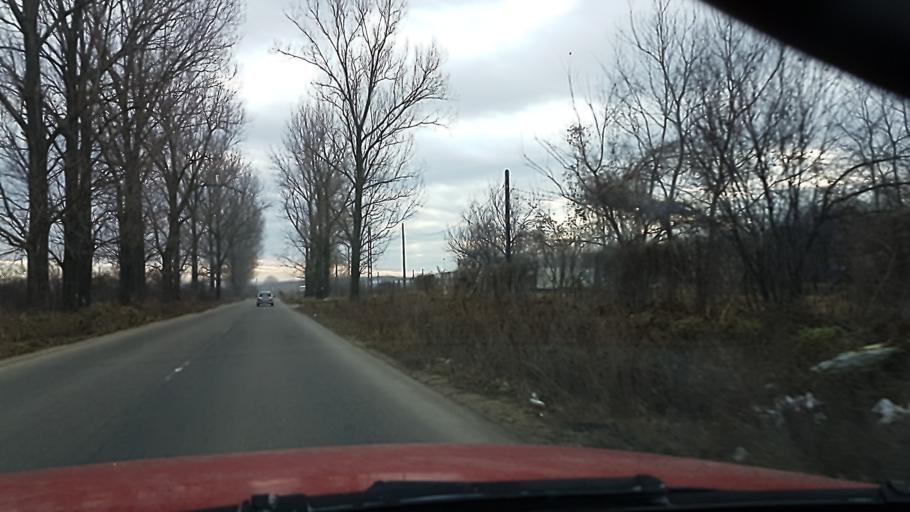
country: RO
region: Giurgiu
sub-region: Comuna Herasti
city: Herasti
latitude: 44.1971
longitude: 26.3646
